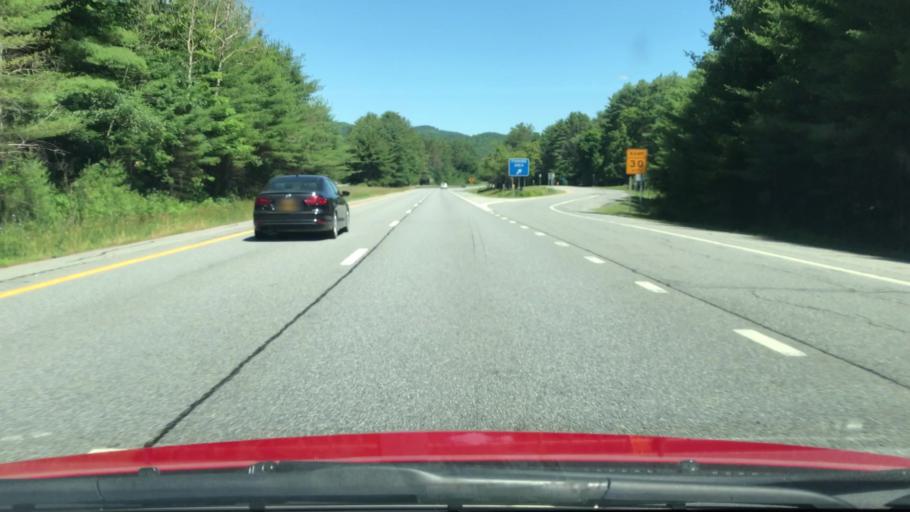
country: US
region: New York
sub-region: Warren County
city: Warrensburg
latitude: 43.5474
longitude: -73.7341
